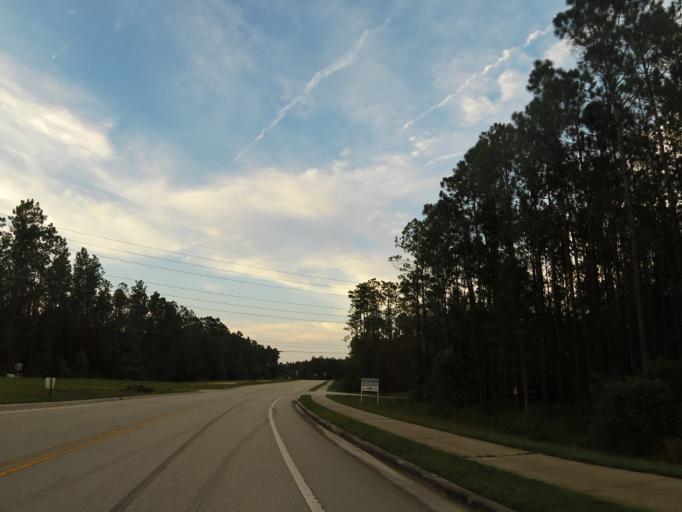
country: US
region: Florida
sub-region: Saint Johns County
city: Fruit Cove
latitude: 30.0731
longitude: -81.6043
